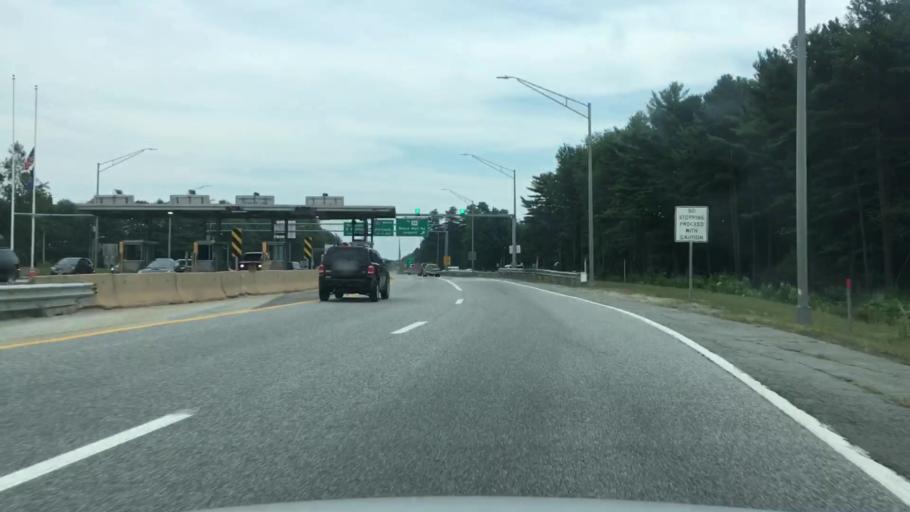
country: US
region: Maine
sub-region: Cumberland County
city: South Portland Gardens
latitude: 43.6302
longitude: -70.3390
